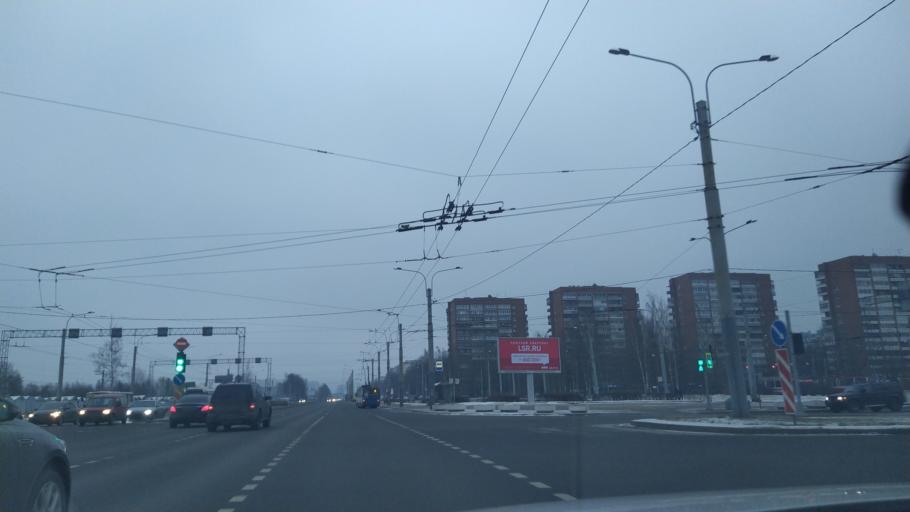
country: RU
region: St.-Petersburg
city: Grazhdanka
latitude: 60.0477
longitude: 30.4050
